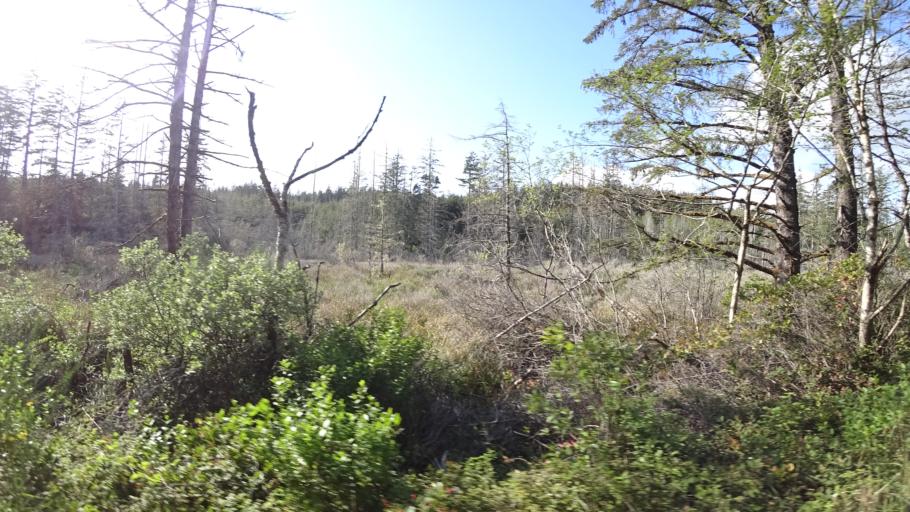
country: US
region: Oregon
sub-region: Douglas County
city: Reedsport
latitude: 43.7485
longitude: -124.1610
